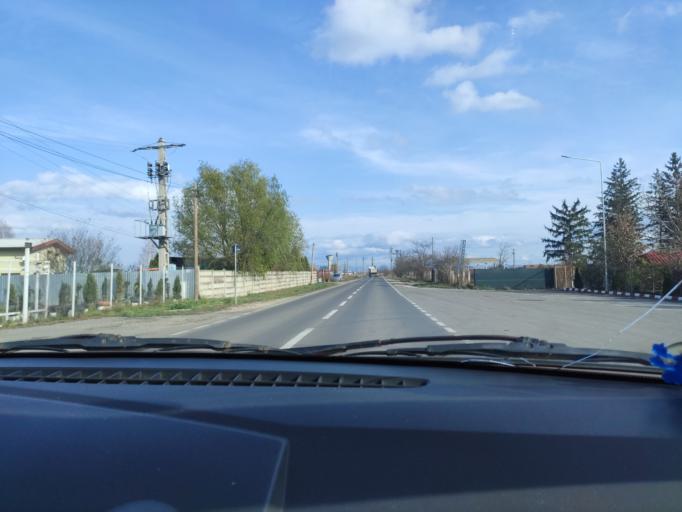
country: RO
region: Brasov
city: Codlea
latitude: 45.7093
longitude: 25.4609
